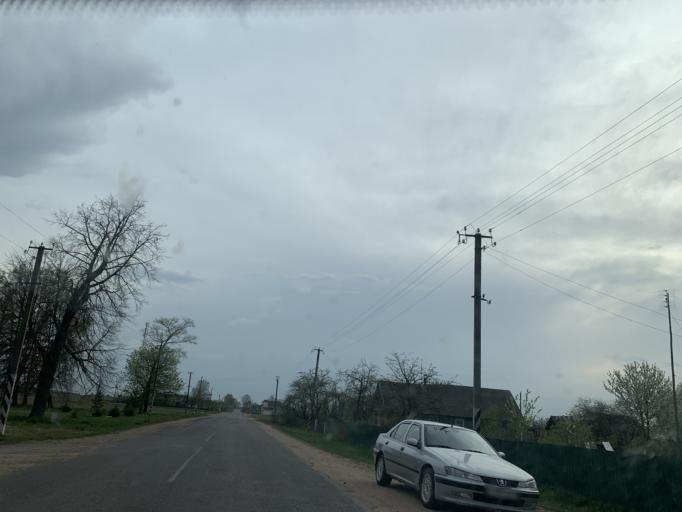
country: BY
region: Minsk
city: Kapyl'
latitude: 53.2810
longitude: 26.9778
